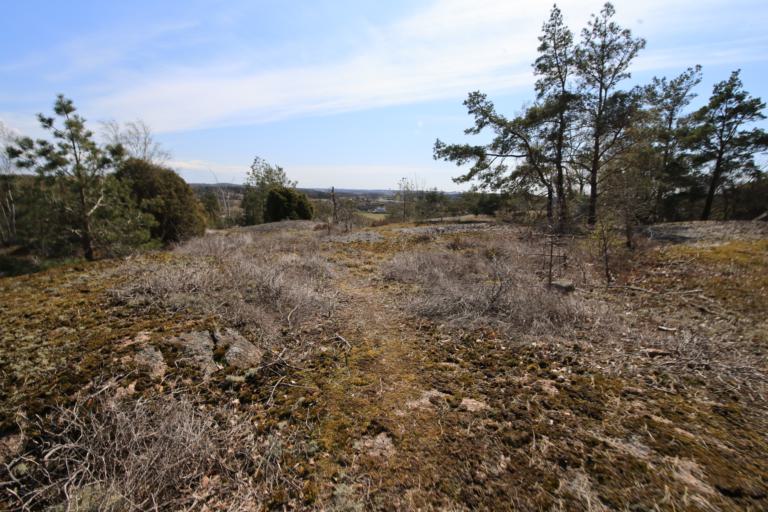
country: SE
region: Halland
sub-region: Varbergs Kommun
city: Varberg
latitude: 57.1720
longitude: 12.2344
